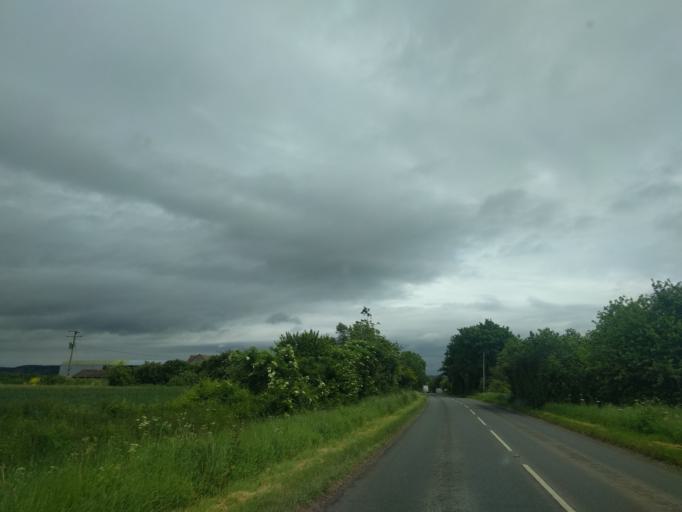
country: GB
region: England
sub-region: Somerset
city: Langport
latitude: 51.0513
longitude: -2.7636
